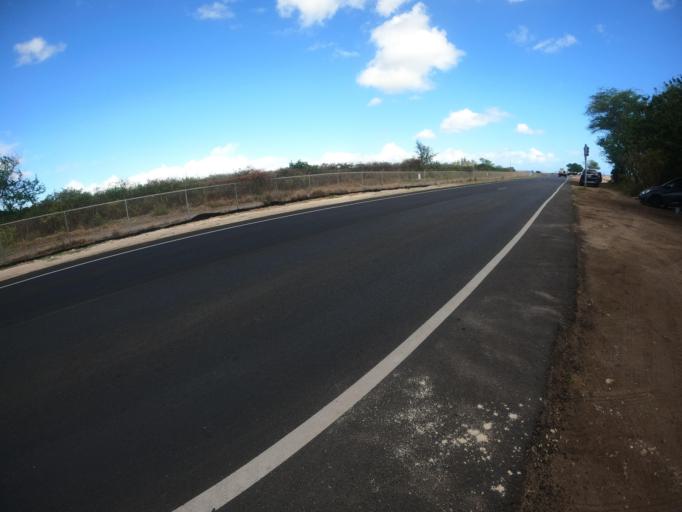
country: US
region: Hawaii
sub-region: Honolulu County
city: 'Ewa Villages
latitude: 21.3007
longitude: -158.0652
